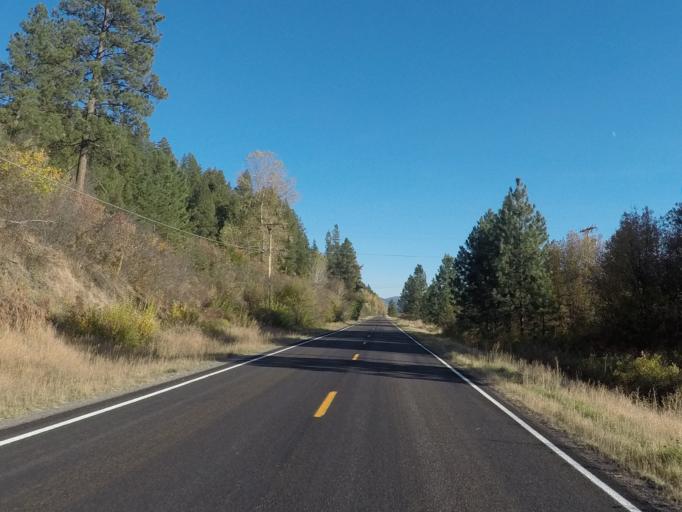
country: US
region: Montana
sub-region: Missoula County
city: Bonner-West Riverside
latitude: 46.8318
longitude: -113.8192
